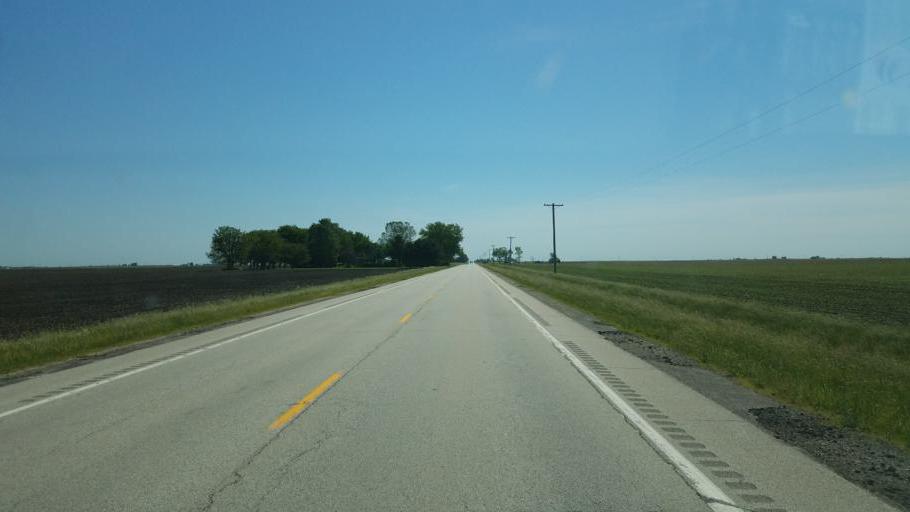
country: US
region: Illinois
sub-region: McLean County
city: Downs
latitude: 40.3122
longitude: -88.8801
